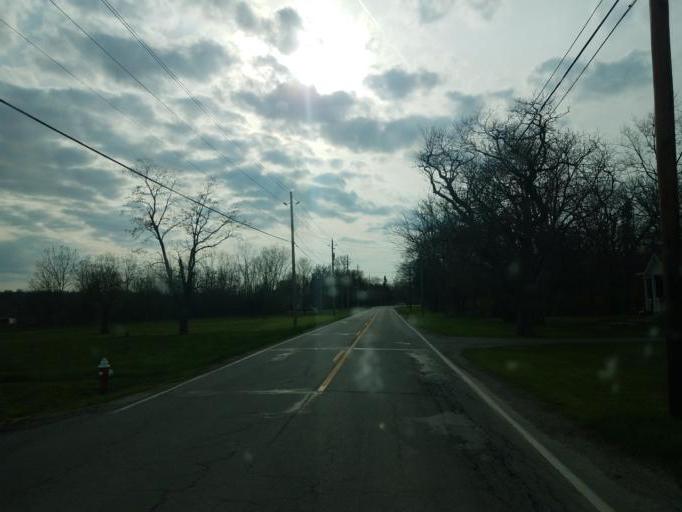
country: US
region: Ohio
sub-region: Erie County
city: Sandusky
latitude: 41.5144
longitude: -82.7515
